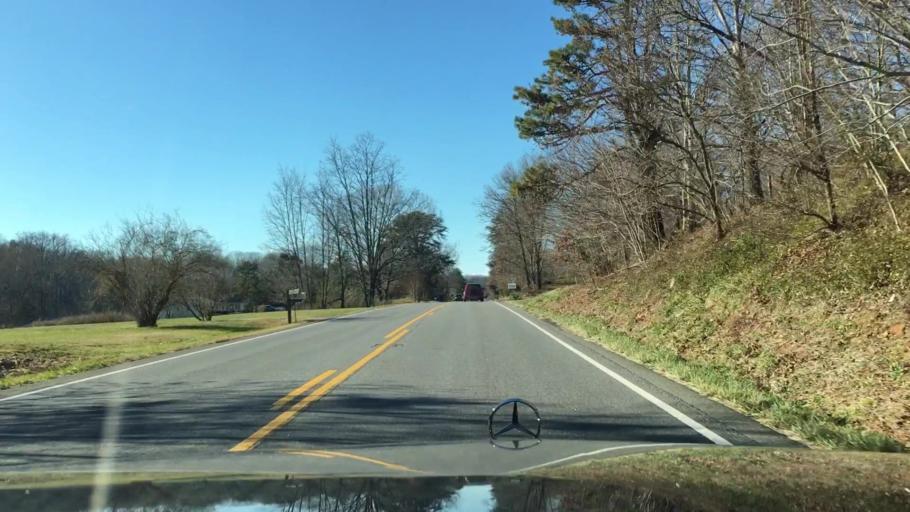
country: US
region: Virginia
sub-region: City of Bedford
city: Bedford
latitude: 37.2398
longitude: -79.5920
